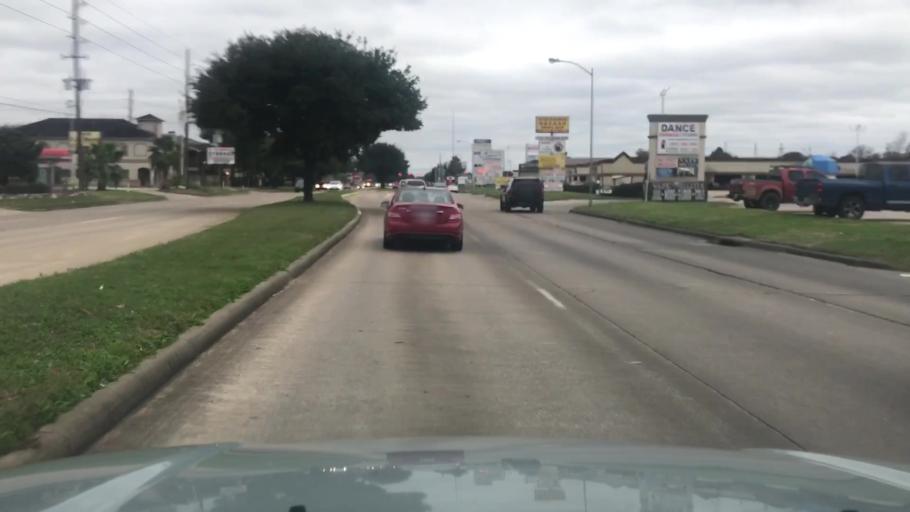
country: US
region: Texas
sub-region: Fort Bend County
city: Cinco Ranch
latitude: 29.7681
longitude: -95.7517
